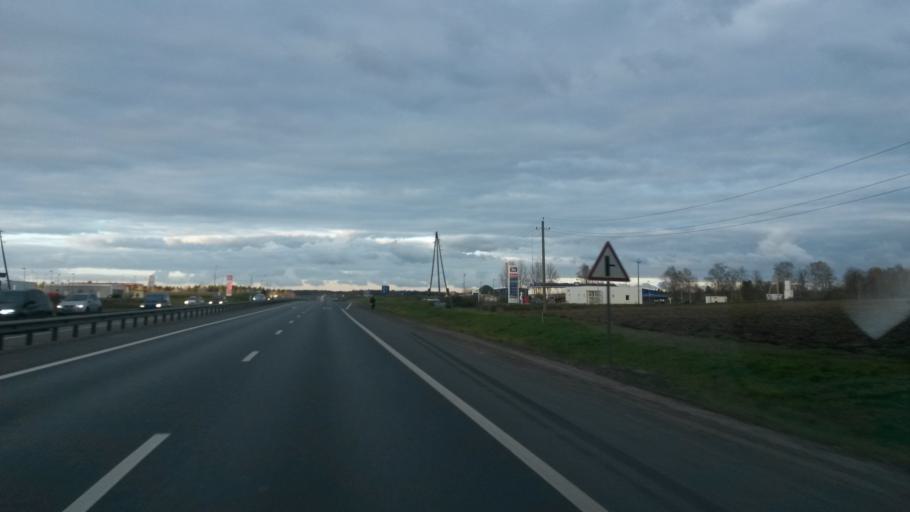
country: RU
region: Moskovskaya
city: Svatkovo
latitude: 56.3187
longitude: 38.2485
